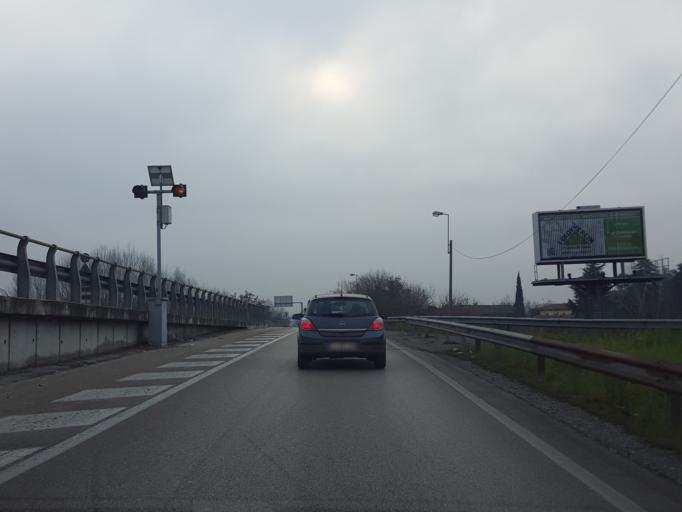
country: IT
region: Veneto
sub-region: Provincia di Vicenza
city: Villaggio Montegrappa
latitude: 45.5382
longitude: 11.5875
